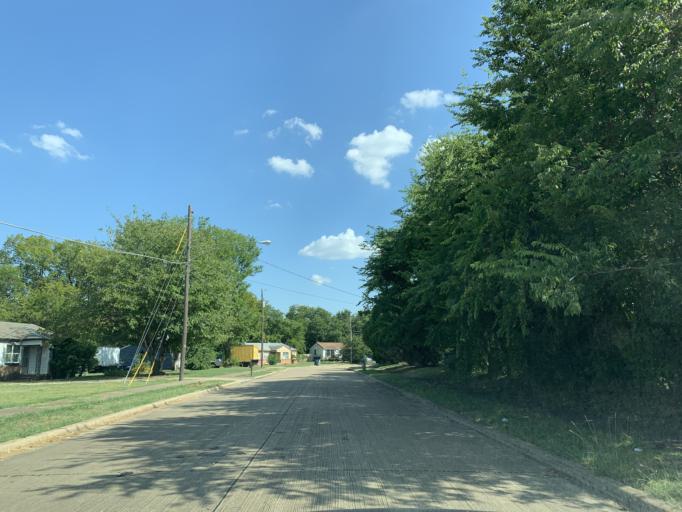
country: US
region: Texas
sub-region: Dallas County
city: Hutchins
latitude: 32.6545
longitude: -96.7683
